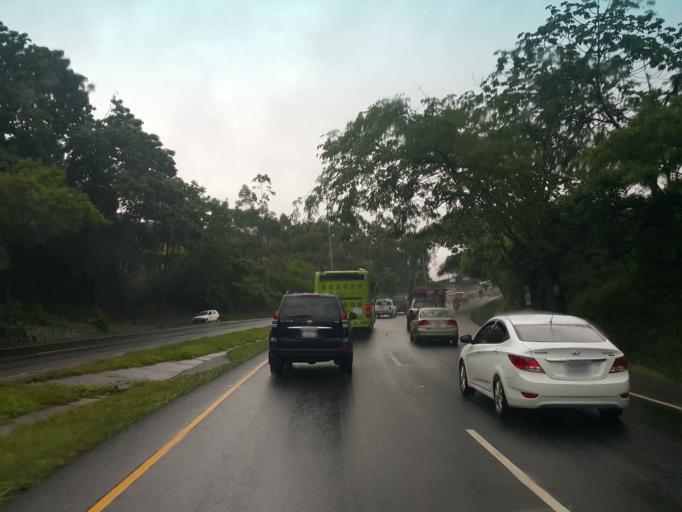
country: CR
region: San Jose
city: Santa Ana
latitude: 9.9476
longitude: -84.1742
